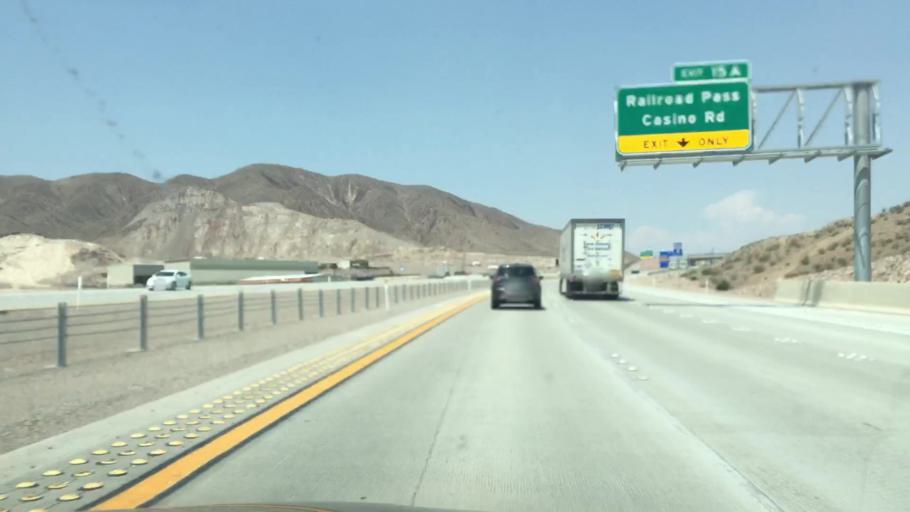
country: US
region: Nevada
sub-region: Clark County
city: Boulder City
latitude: 35.9586
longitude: -114.9096
